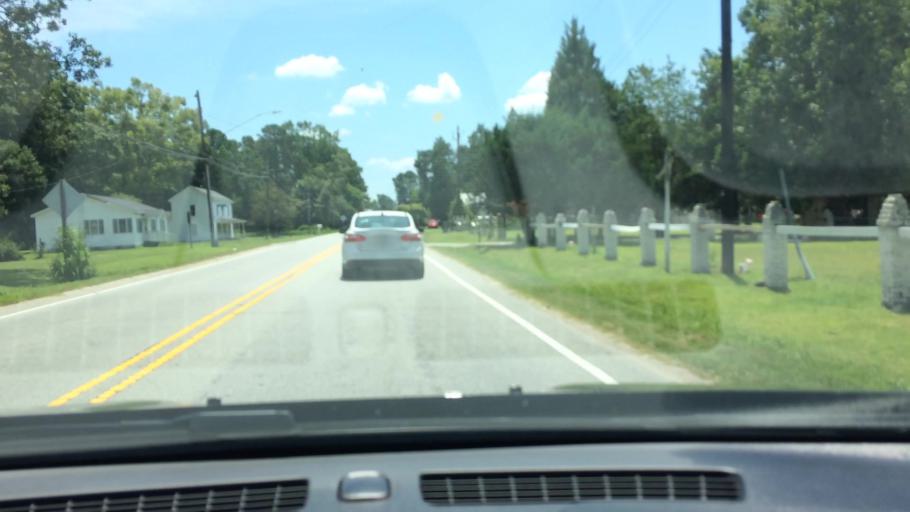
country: US
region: North Carolina
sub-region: Beaufort County
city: Washington
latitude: 35.5670
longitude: -77.1991
